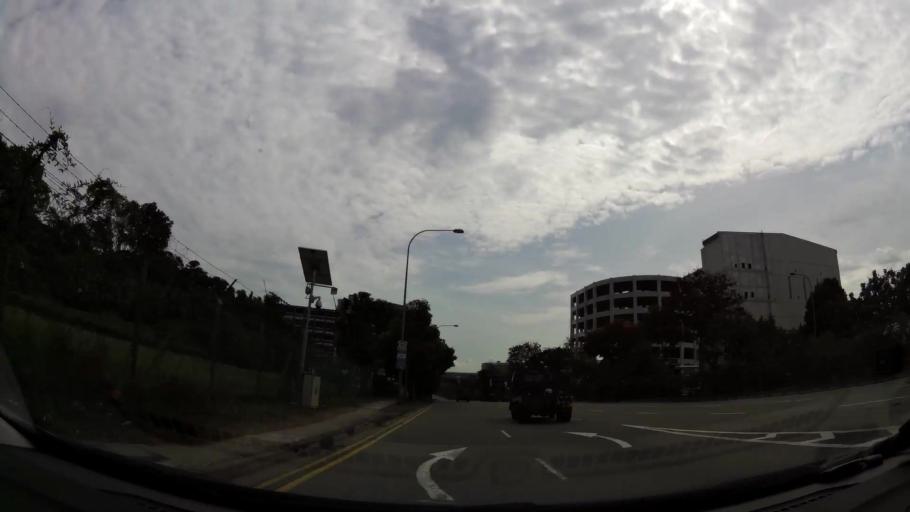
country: SG
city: Singapore
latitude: 1.3144
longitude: 103.7115
